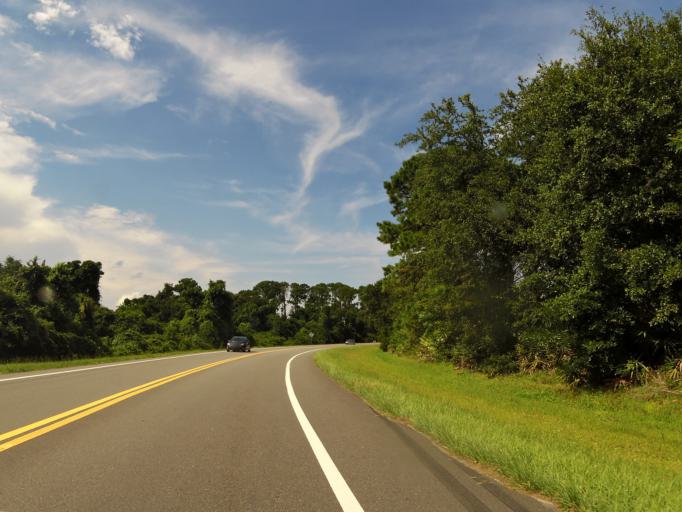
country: US
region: Florida
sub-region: Nassau County
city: Fernandina Beach
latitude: 30.6017
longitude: -81.4592
